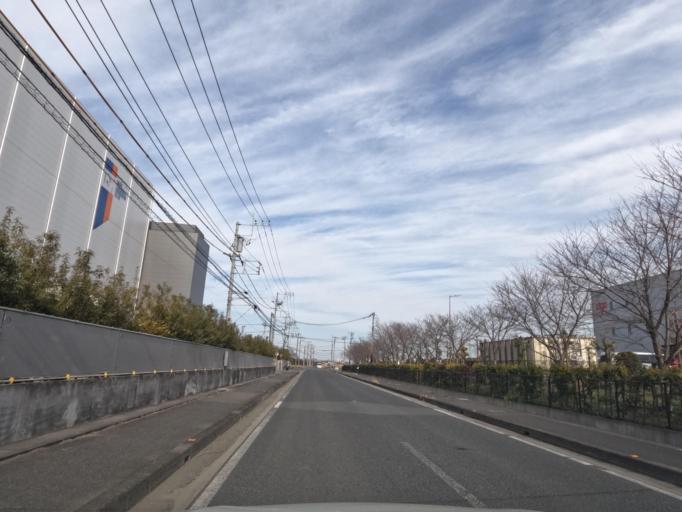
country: JP
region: Saitama
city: Kasukabe
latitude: 35.9519
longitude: 139.7332
